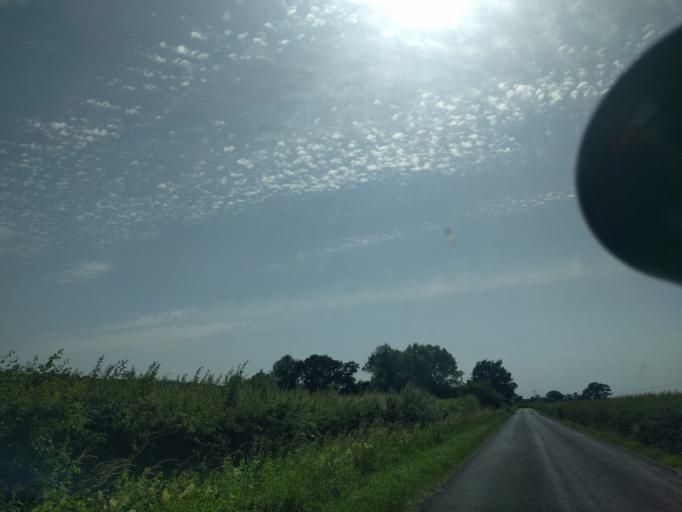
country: GB
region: England
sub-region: Wiltshire
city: Lyneham
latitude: 51.5381
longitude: -1.9764
